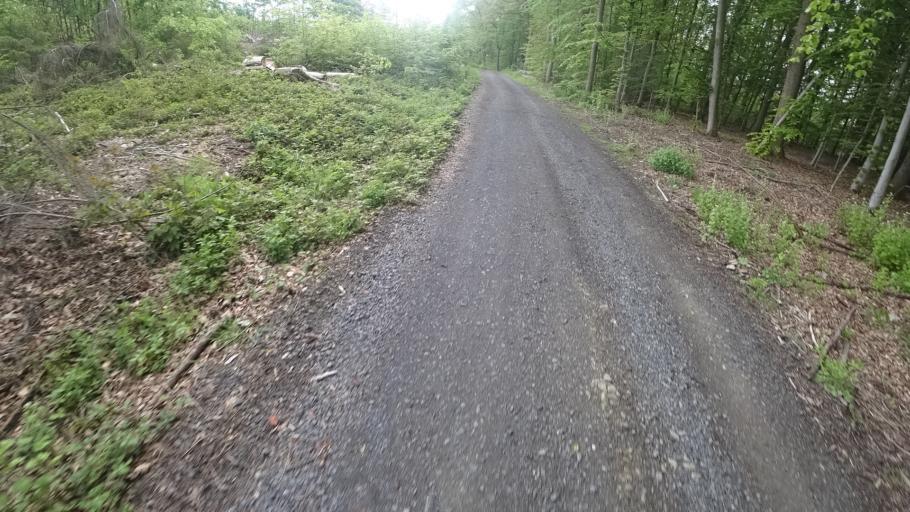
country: DE
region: Rheinland-Pfalz
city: Scheuerfeld
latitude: 50.7782
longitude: 7.8416
